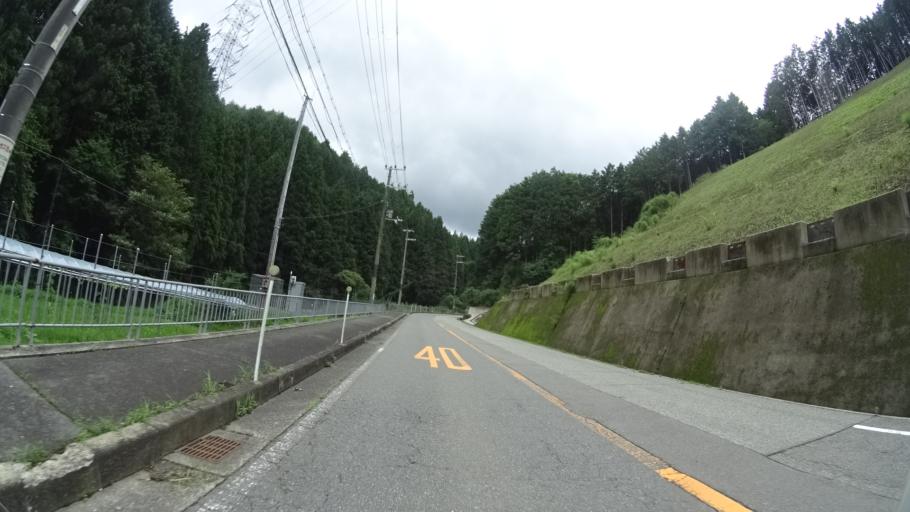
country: JP
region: Kyoto
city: Kameoka
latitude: 34.9684
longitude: 135.4792
